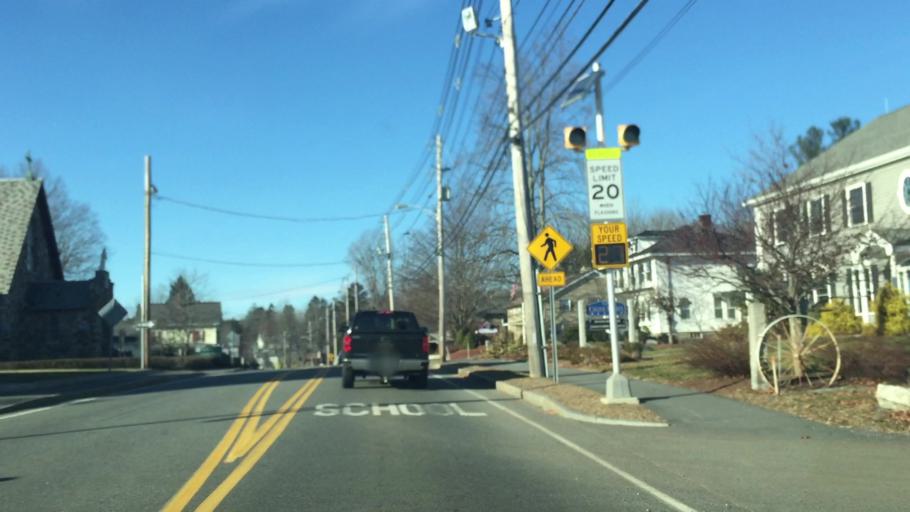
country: US
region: New Hampshire
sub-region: Rockingham County
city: Salem
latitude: 42.7824
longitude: -71.2331
